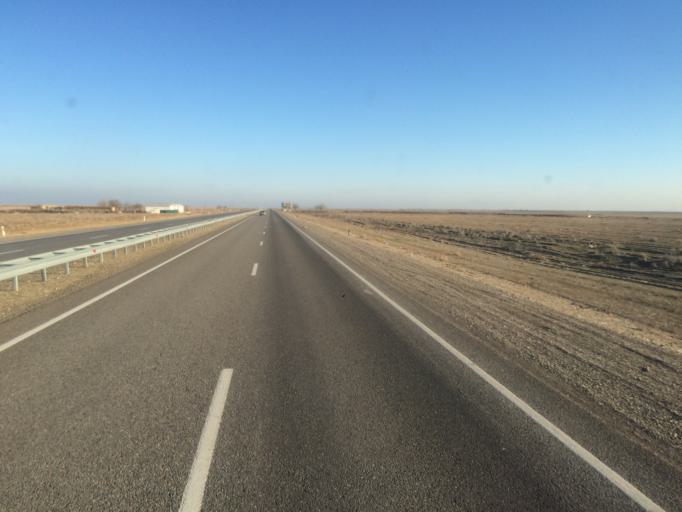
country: KZ
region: Ongtustik Qazaqstan
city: Turkestan
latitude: 43.5296
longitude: 67.7854
